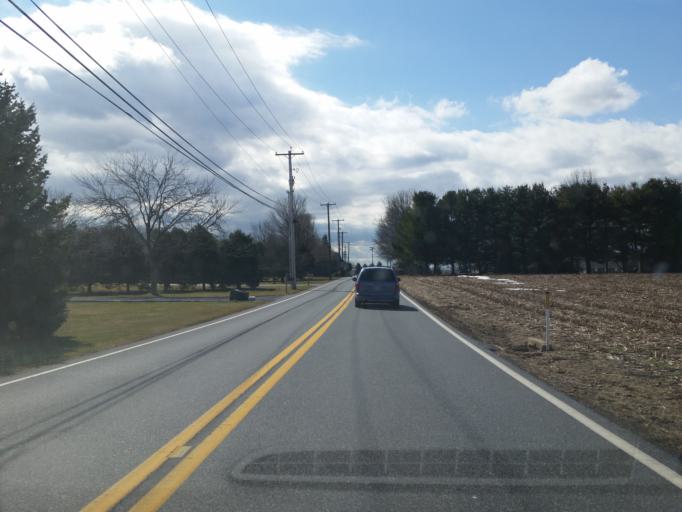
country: US
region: Pennsylvania
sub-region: Lebanon County
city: Campbelltown
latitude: 40.2944
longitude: -76.5672
